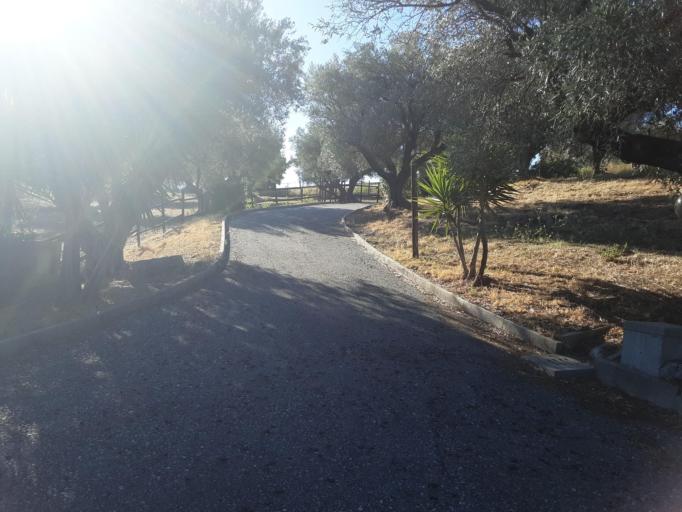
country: IT
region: Calabria
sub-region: Provincia di Catanzaro
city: Staletti
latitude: 38.7650
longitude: 16.5538
